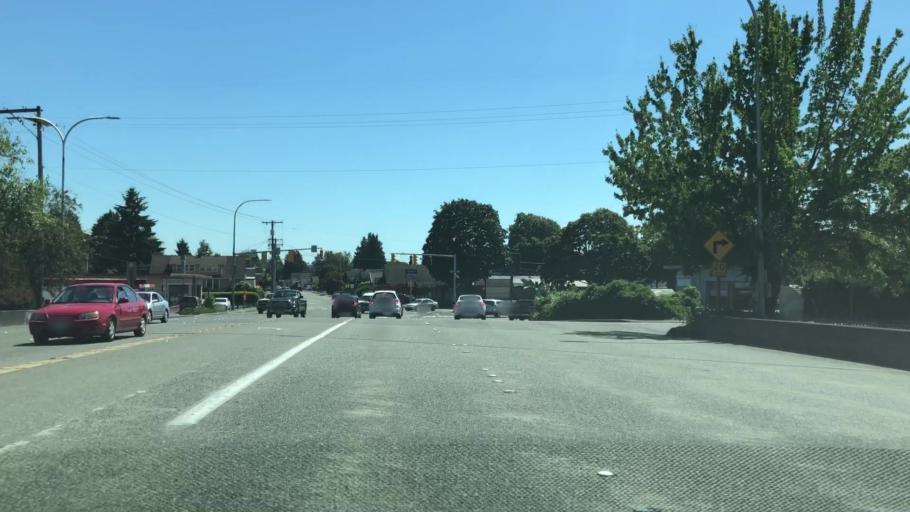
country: US
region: Washington
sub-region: King County
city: Renton
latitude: 47.4858
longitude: -122.2091
